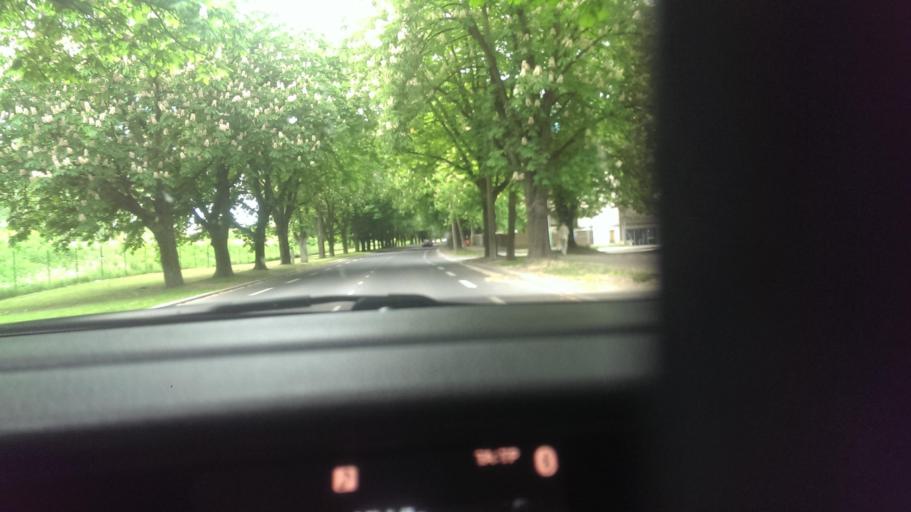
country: EE
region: Harju
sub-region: Tallinna linn
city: Tallinn
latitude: 59.4220
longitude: 24.7352
